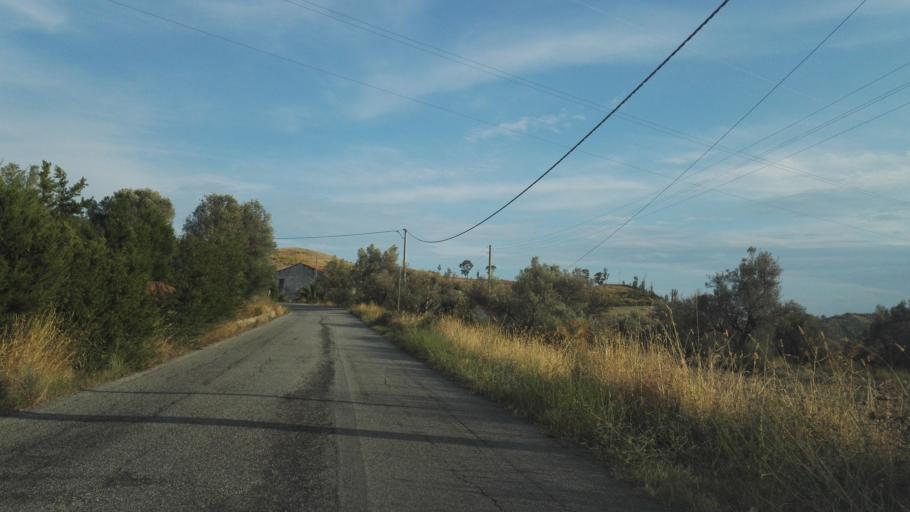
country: IT
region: Calabria
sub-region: Provincia di Reggio Calabria
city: Placanica
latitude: 38.3898
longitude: 16.4698
